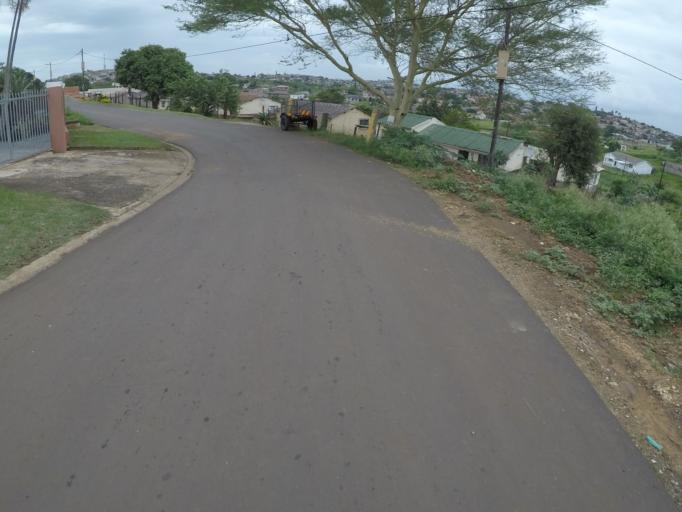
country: ZA
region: KwaZulu-Natal
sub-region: uThungulu District Municipality
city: Empangeni
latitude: -28.7756
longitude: 31.8599
